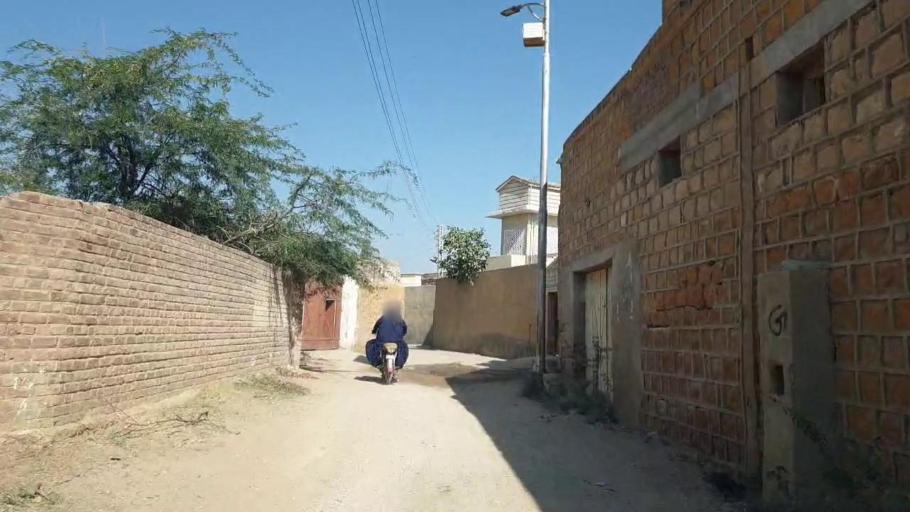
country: PK
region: Sindh
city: Jamshoro
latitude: 25.3589
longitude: 67.8328
